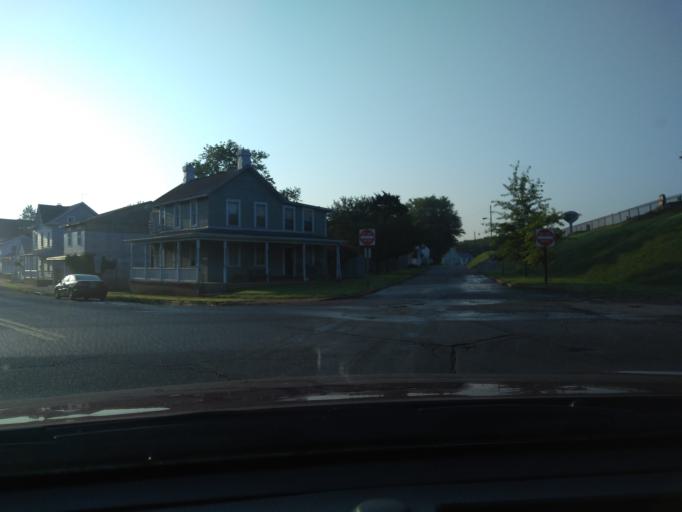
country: US
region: Maryland
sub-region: Washington County
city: Williamsport
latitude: 39.5992
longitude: -77.8250
